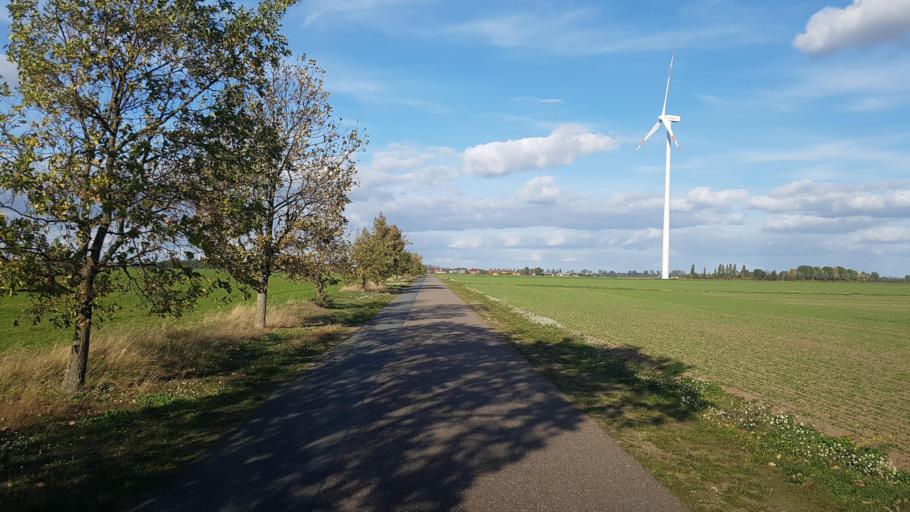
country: DE
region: Brandenburg
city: Bad Liebenwerda
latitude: 51.4762
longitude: 13.3294
